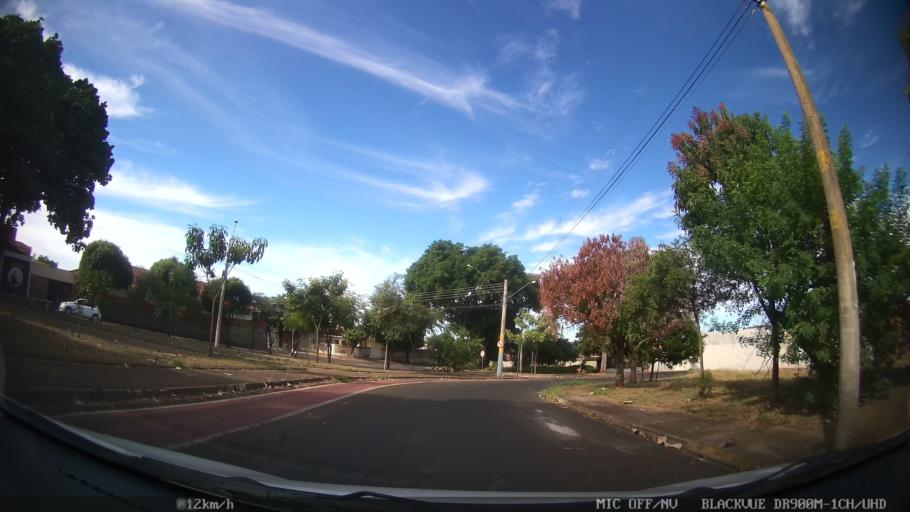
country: BR
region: Sao Paulo
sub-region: Catanduva
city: Catanduva
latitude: -21.1158
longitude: -48.9685
